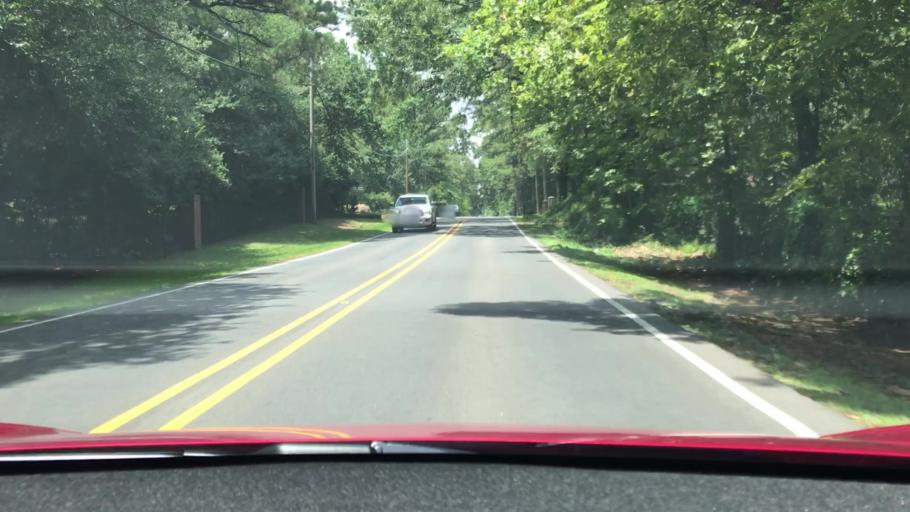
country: US
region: Louisiana
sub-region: Bossier Parish
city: Bossier City
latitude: 32.3750
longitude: -93.7137
